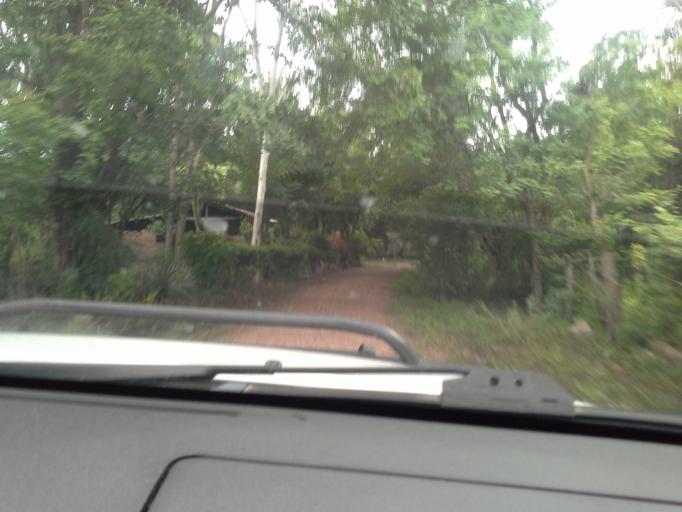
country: NI
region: Matagalpa
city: Ciudad Dario
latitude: 12.8232
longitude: -86.1905
